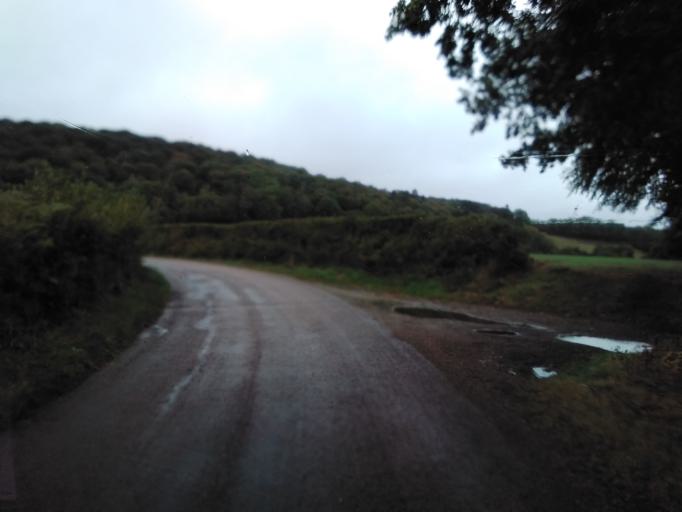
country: FR
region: Bourgogne
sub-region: Departement de la Nievre
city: Lormes
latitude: 47.2855
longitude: 3.9815
